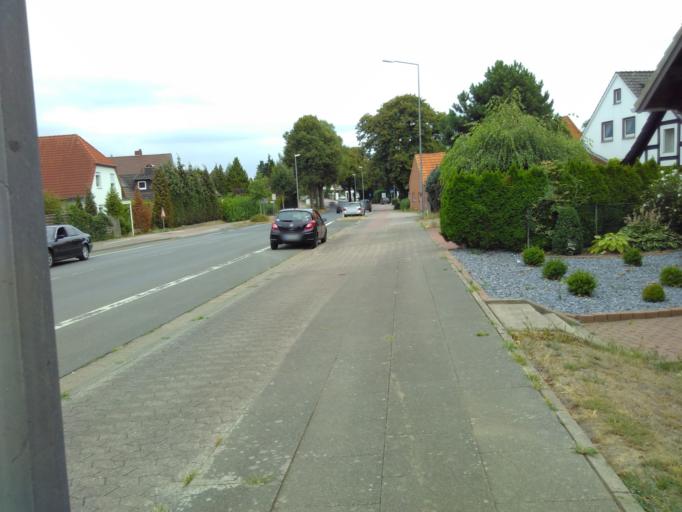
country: DE
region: North Rhine-Westphalia
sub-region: Regierungsbezirk Detmold
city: Minden
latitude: 52.2963
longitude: 8.8680
